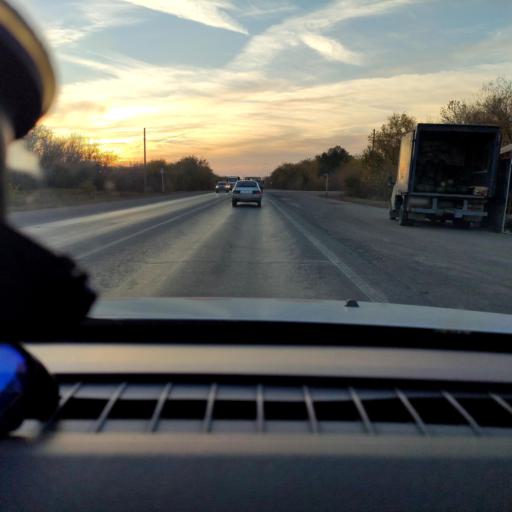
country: RU
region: Samara
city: Samara
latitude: 53.0809
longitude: 50.1006
